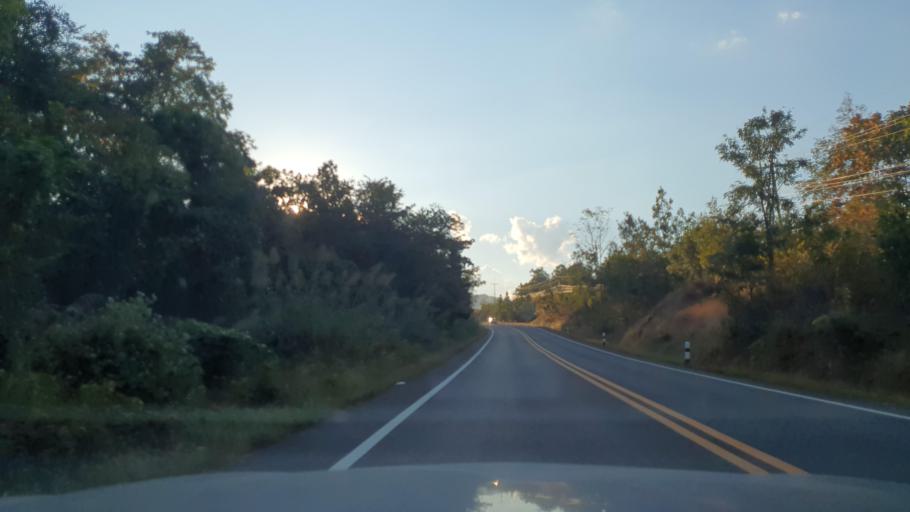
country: TH
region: Phayao
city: Chiang Muan
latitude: 18.9262
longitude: 100.2186
